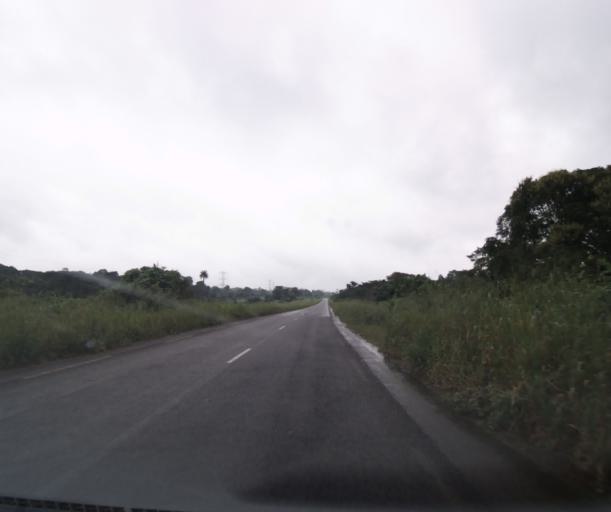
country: CM
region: Littoral
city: Edea
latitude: 3.4879
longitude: 10.1258
